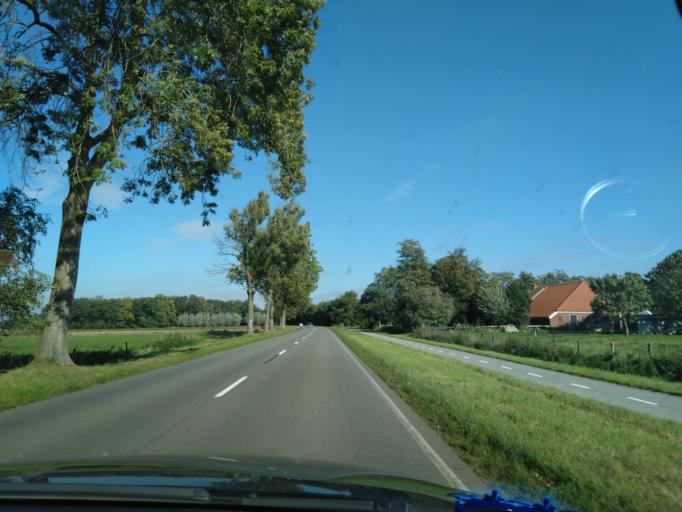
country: NL
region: Drenthe
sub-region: Gemeente Aa en Hunze
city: Anloo
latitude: 53.0634
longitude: 6.7520
